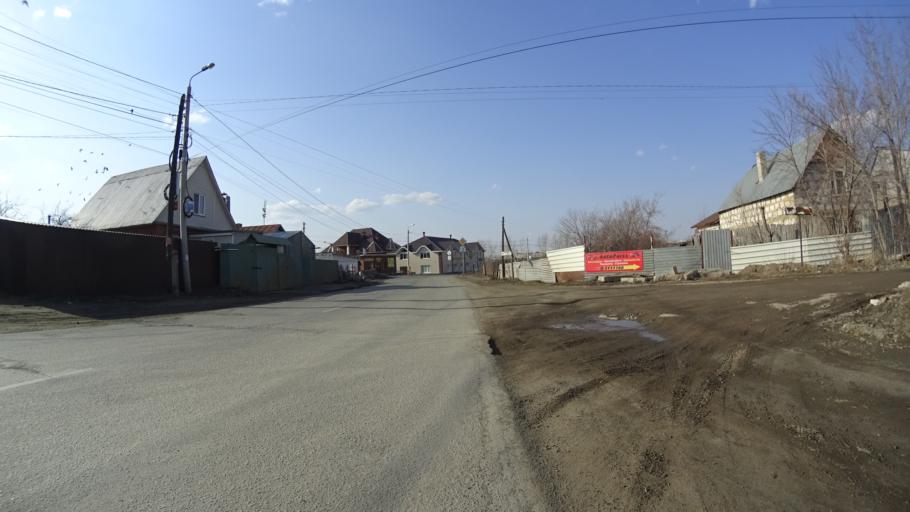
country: RU
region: Chelyabinsk
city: Novosineglazovskiy
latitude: 55.1104
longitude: 61.3327
